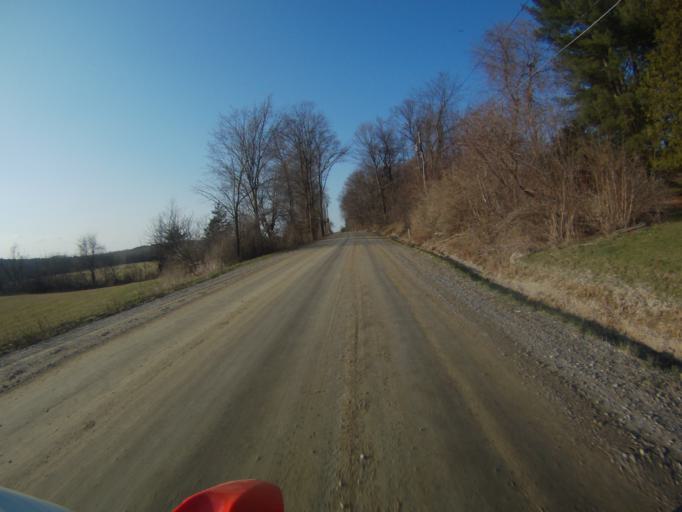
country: US
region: Vermont
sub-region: Addison County
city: Bristol
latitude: 44.1055
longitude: -73.0888
